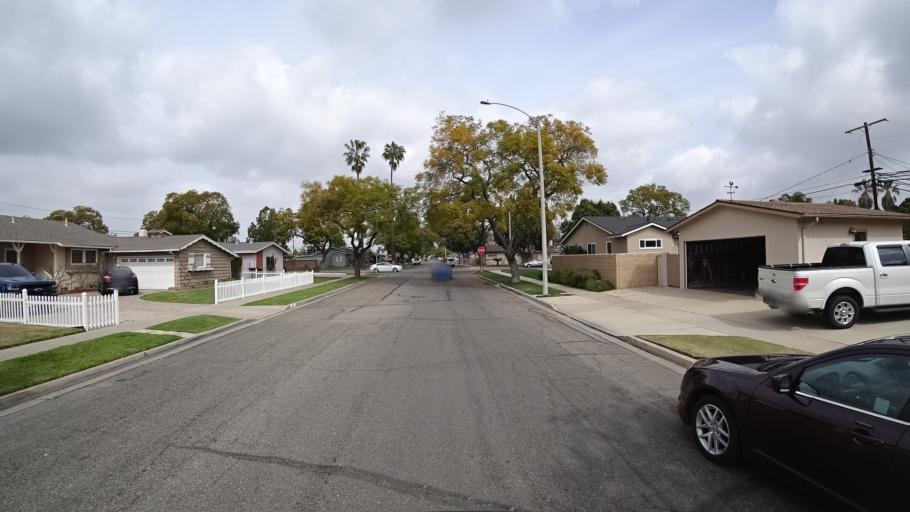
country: US
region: California
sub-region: Orange County
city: Stanton
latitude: 33.8260
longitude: -118.0010
